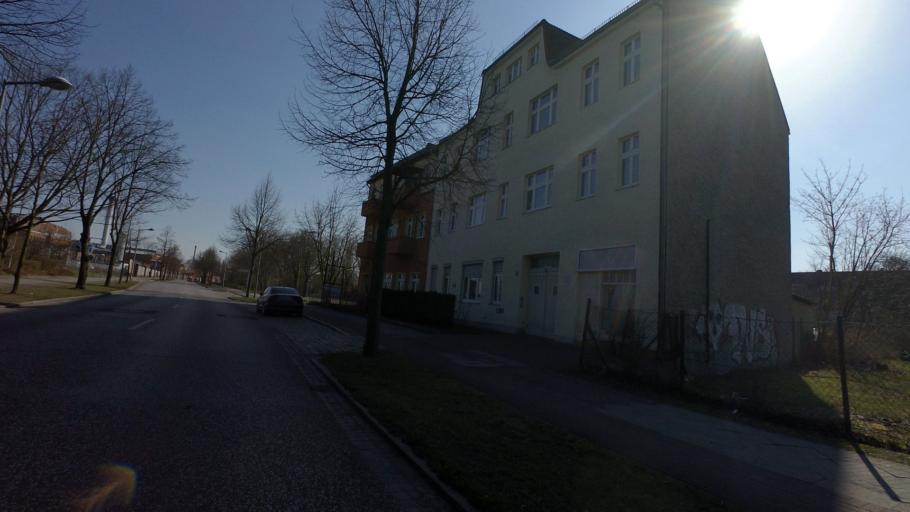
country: DE
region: Brandenburg
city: Hennigsdorf
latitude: 52.6329
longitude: 13.2063
